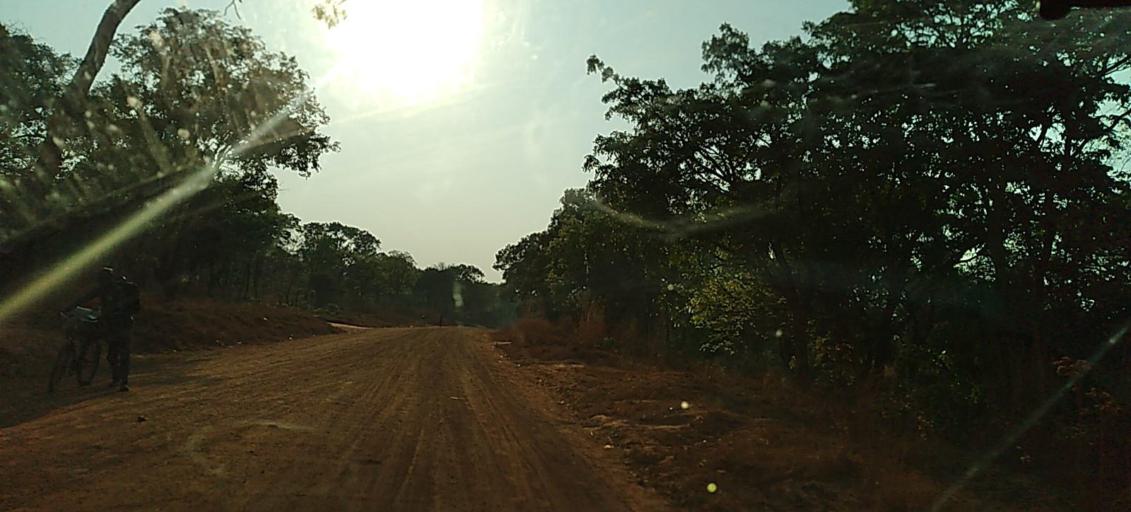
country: ZM
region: North-Western
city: Kasempa
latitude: -13.4720
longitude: 25.8696
